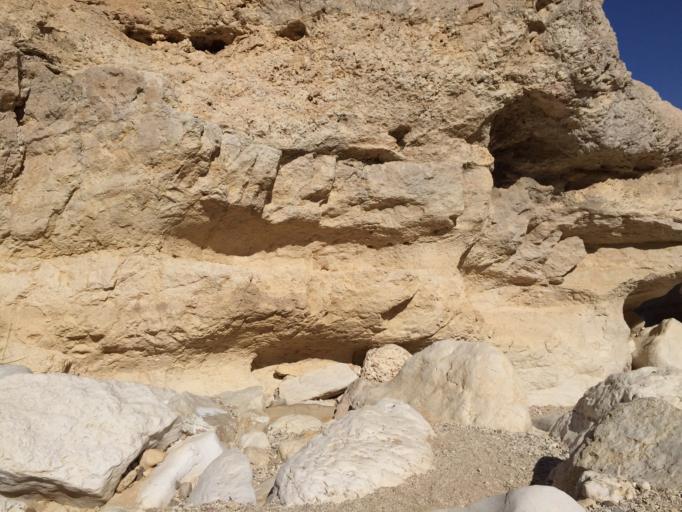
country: IL
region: Southern District
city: Mitzpe Ramon
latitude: 30.5982
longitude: 34.9454
